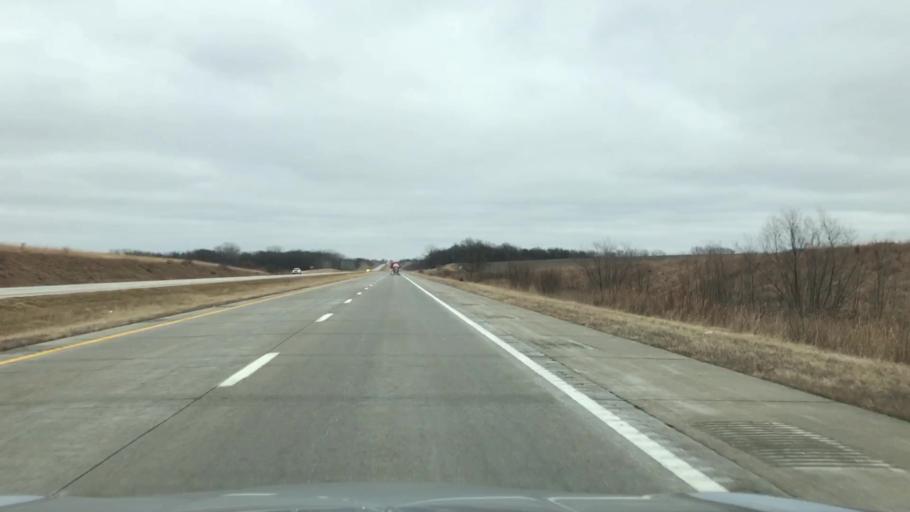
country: US
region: Missouri
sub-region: Caldwell County
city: Hamilton
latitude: 39.7340
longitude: -93.9771
